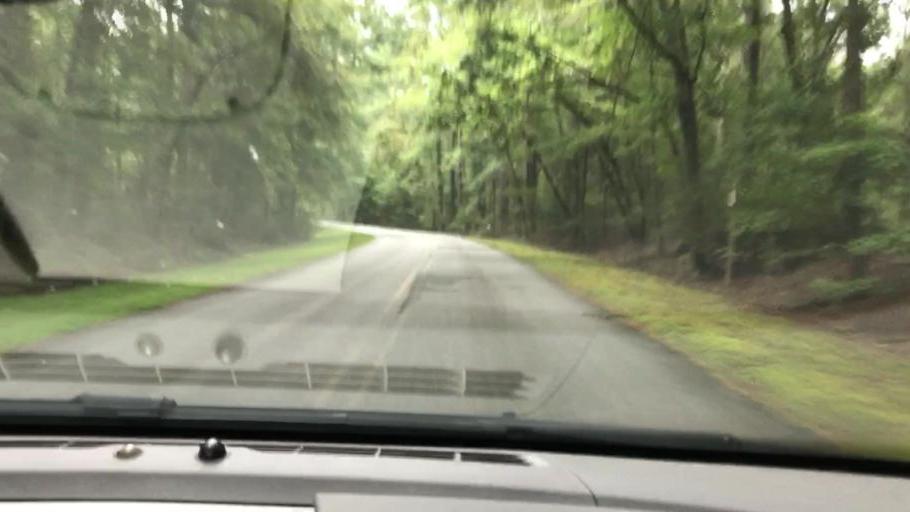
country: US
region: Georgia
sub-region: Clay County
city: Fort Gaines
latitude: 31.6670
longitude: -85.0558
